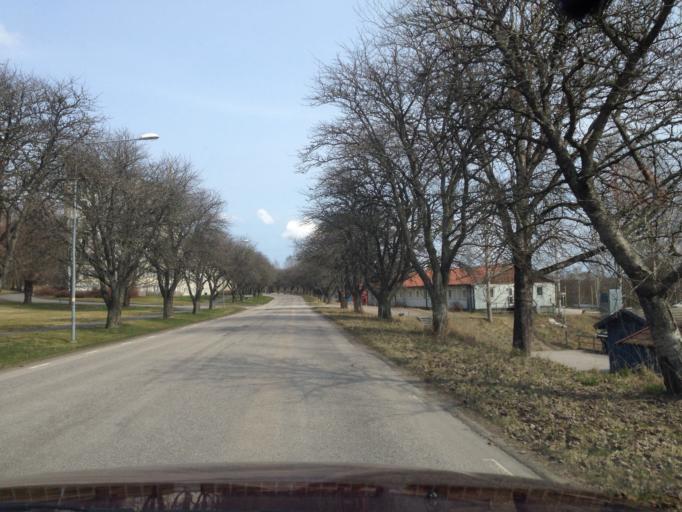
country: SE
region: Dalarna
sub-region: Ludvika Kommun
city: Grangesberg
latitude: 60.0786
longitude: 14.9878
